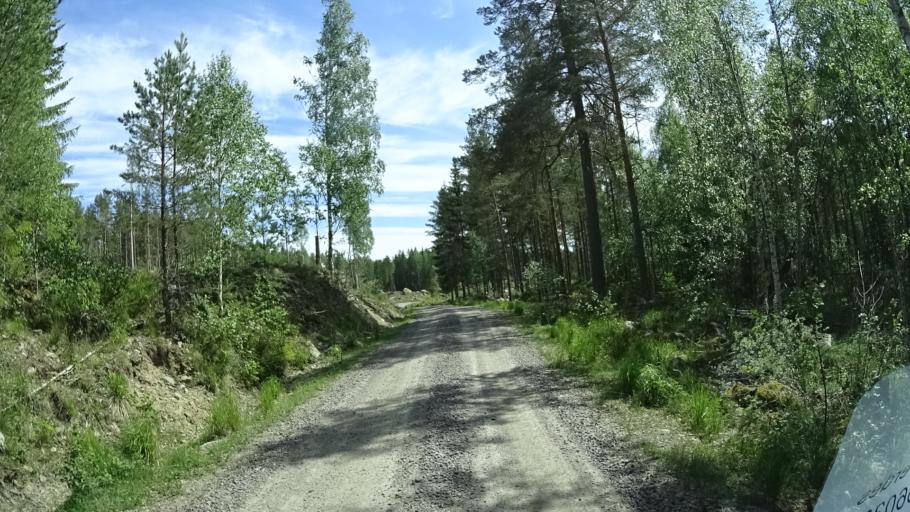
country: SE
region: OEstergoetland
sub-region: Norrkopings Kommun
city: Svartinge
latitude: 58.7806
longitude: 15.9242
